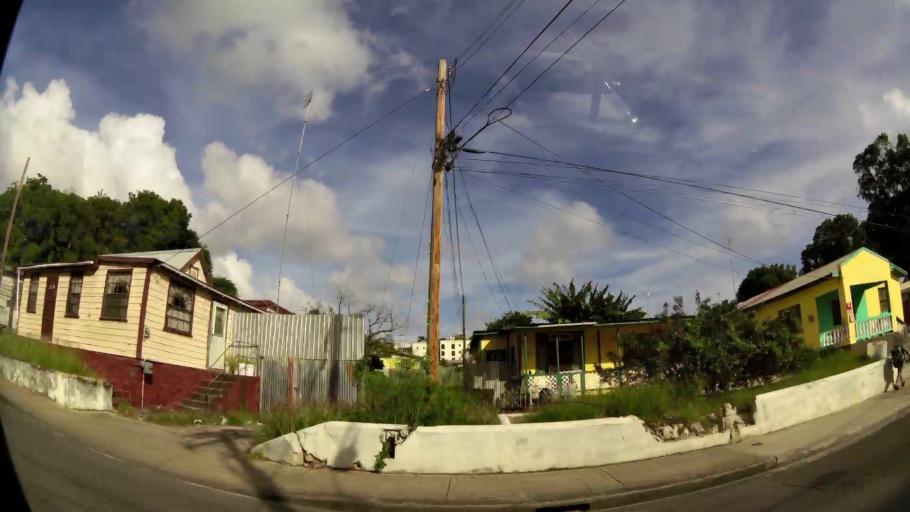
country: BB
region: Saint Michael
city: Bridgetown
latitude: 13.0864
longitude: -59.6008
